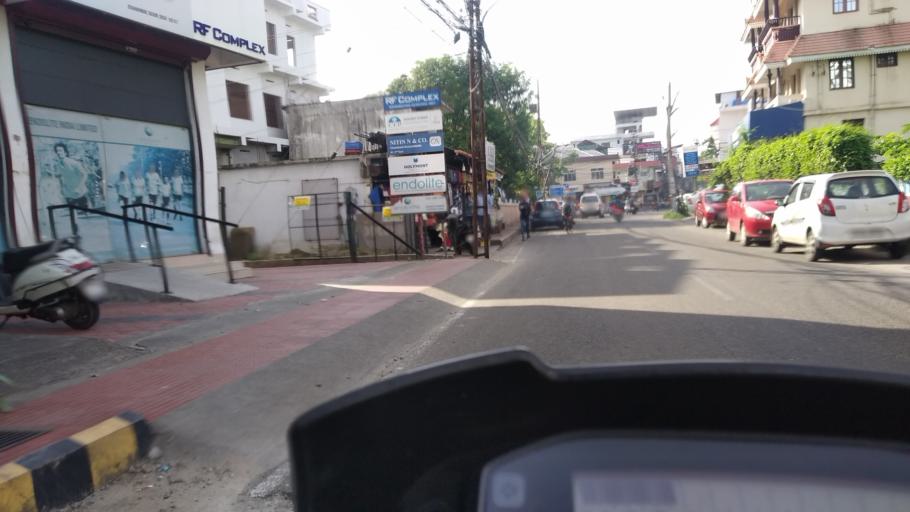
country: IN
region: Kerala
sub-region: Ernakulam
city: Elur
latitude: 10.0016
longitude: 76.2959
